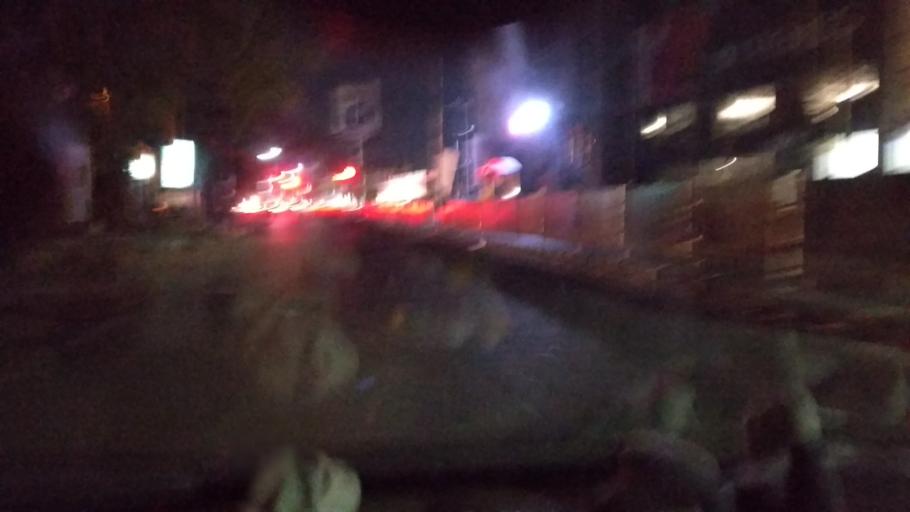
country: IN
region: Telangana
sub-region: Hyderabad
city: Malkajgiri
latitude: 17.4405
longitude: 78.4942
